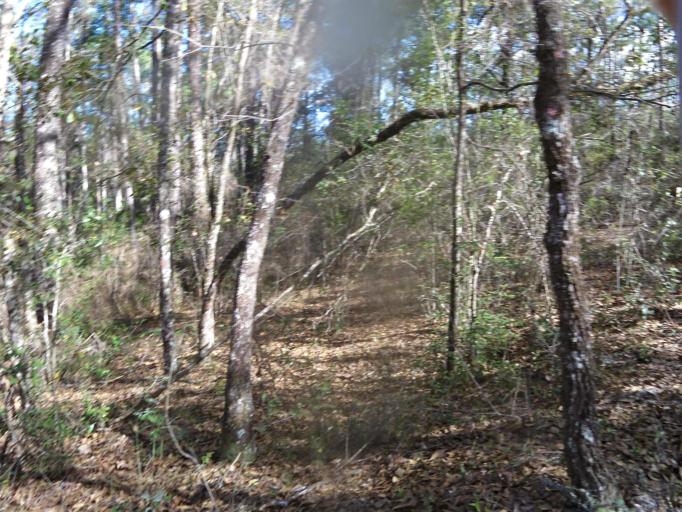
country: US
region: Florida
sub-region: Clay County
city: Middleburg
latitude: 30.1519
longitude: -81.9649
